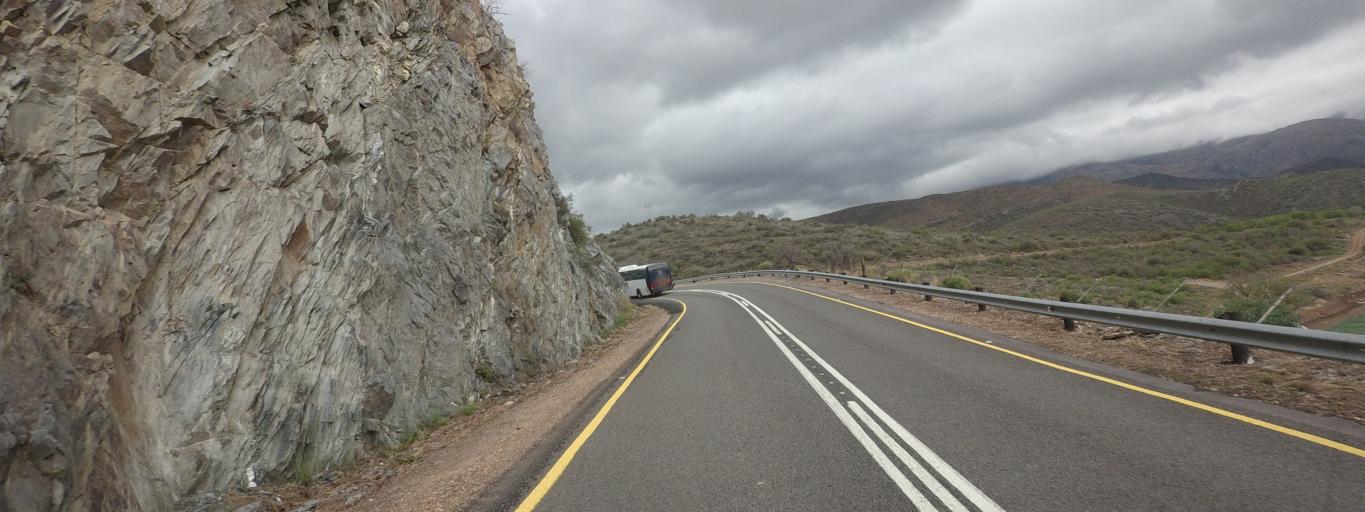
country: ZA
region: Western Cape
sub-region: Eden District Municipality
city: Oudtshoorn
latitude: -33.4176
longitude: 22.2386
